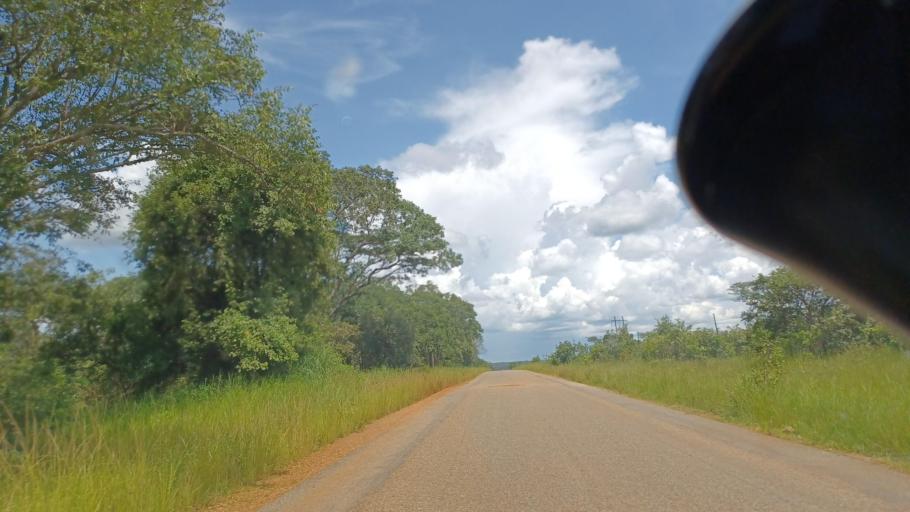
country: ZM
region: North-Western
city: Solwezi
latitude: -12.6084
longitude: 26.1245
